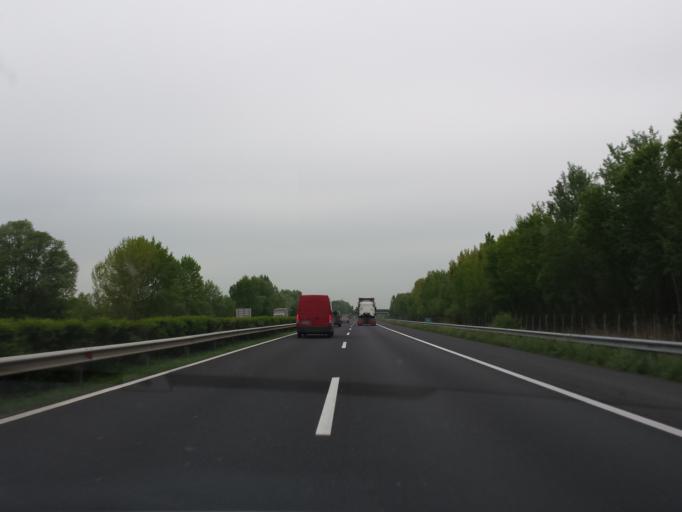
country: HU
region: Gyor-Moson-Sopron
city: Kimle
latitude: 47.7950
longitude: 17.3175
